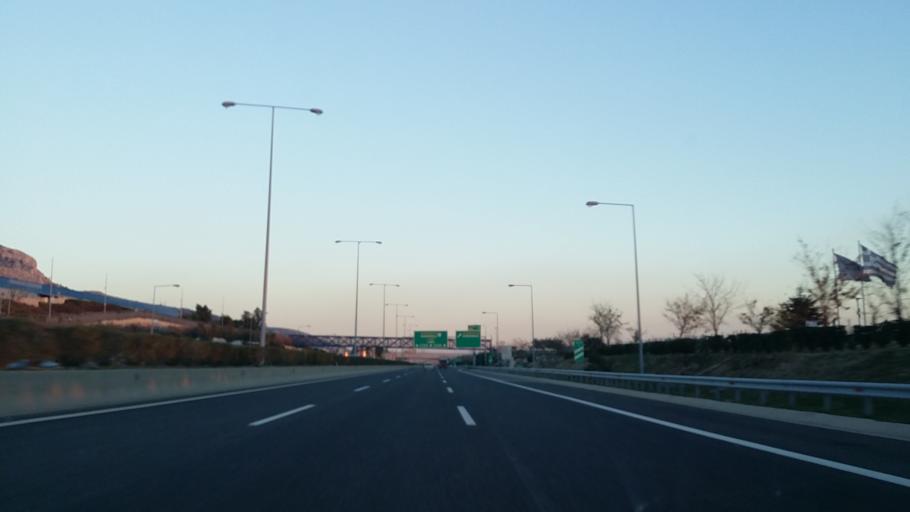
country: GR
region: Attica
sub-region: Nomarchia Dytikis Attikis
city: Aspropyrgos
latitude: 38.0912
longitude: 23.6141
